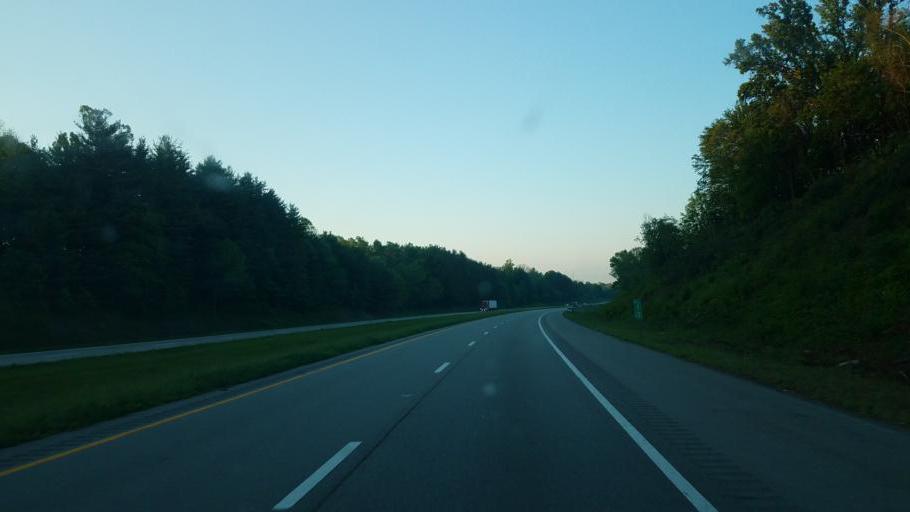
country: US
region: Ohio
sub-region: Washington County
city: Devola
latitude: 39.5815
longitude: -81.4568
